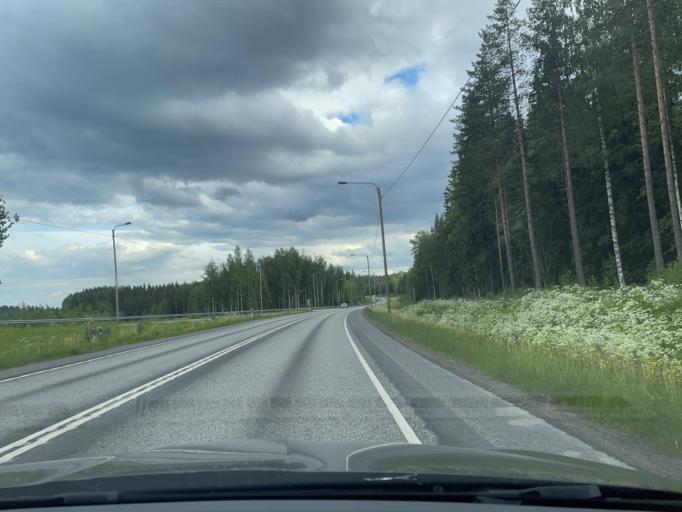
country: FI
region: Central Finland
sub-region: Jyvaeskylae
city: Jyvaeskylae
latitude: 62.2479
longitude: 25.6501
